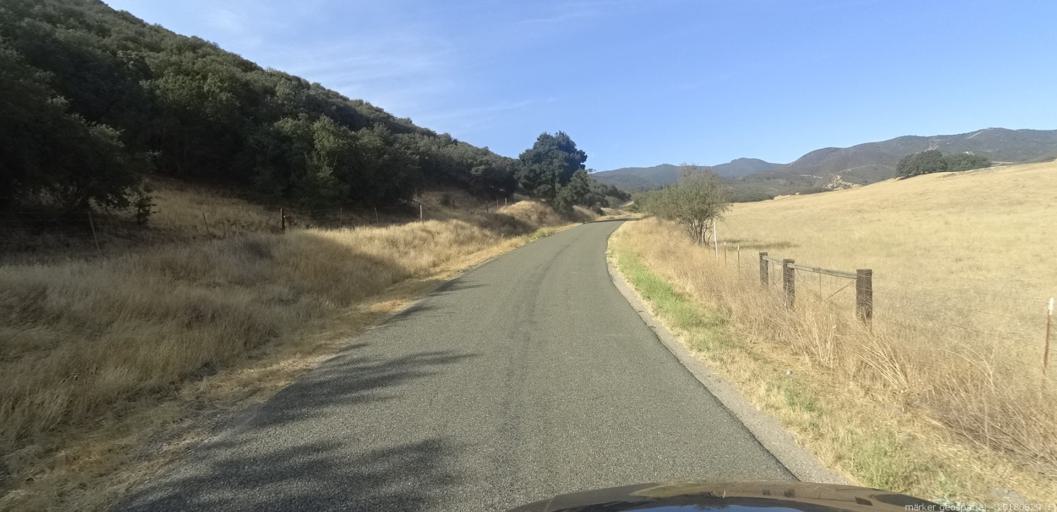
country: US
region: California
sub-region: Monterey County
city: King City
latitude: 36.0587
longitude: -121.0486
